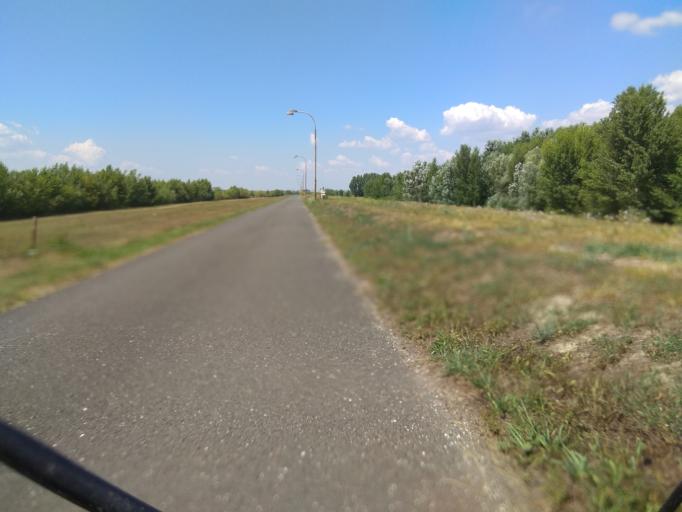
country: SK
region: Trnavsky
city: Gabcikovo
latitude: 47.8600
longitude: 17.5656
